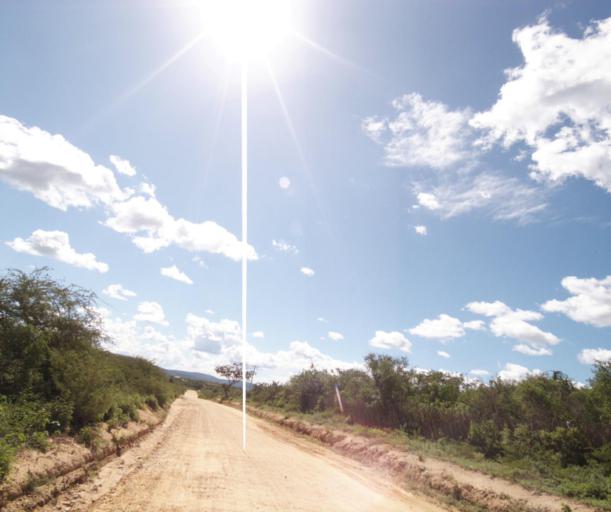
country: BR
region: Bahia
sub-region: Pocoes
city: Pocoes
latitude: -14.2551
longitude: -40.7267
